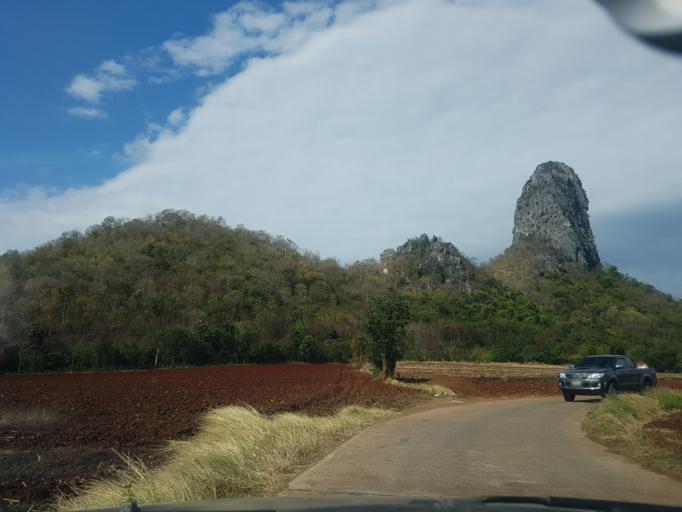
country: TH
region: Sara Buri
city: Phra Phutthabat
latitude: 14.8289
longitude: 100.7611
